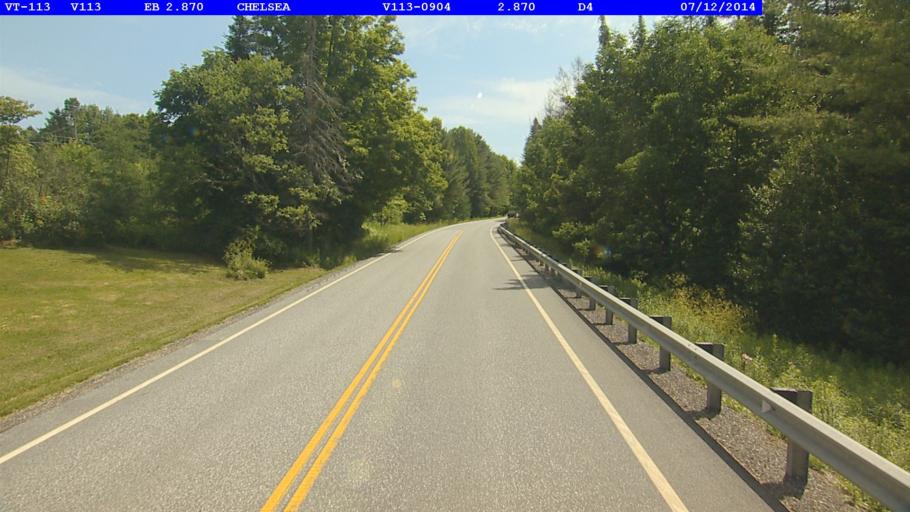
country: US
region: Vermont
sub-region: Orange County
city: Chelsea
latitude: 43.9920
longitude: -72.3956
